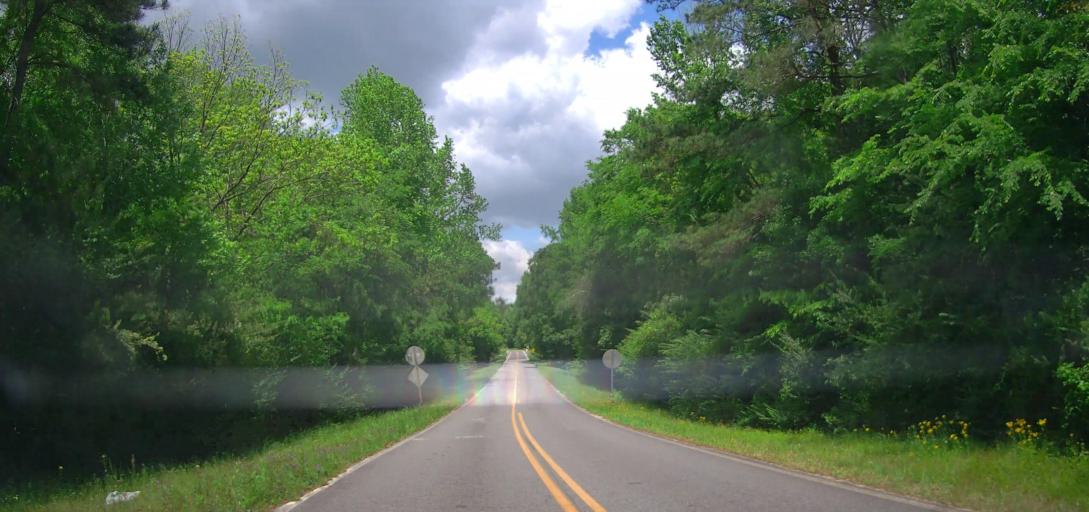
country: US
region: Georgia
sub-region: Laurens County
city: East Dublin
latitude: 32.5953
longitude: -82.7993
